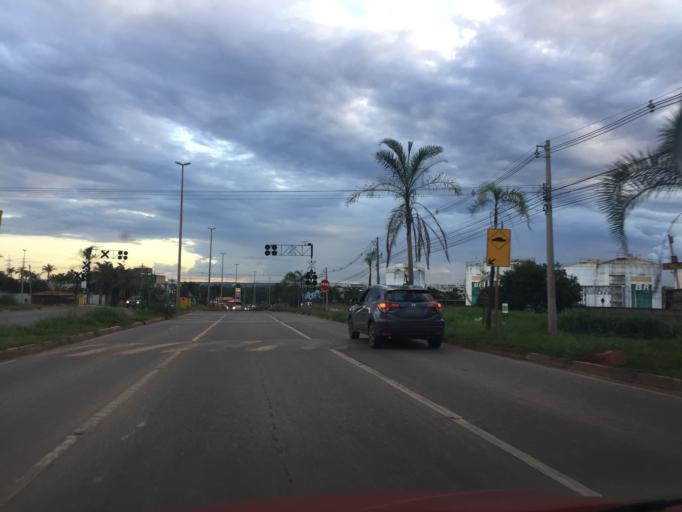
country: BR
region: Federal District
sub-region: Brasilia
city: Brasilia
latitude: -15.7985
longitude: -47.9713
